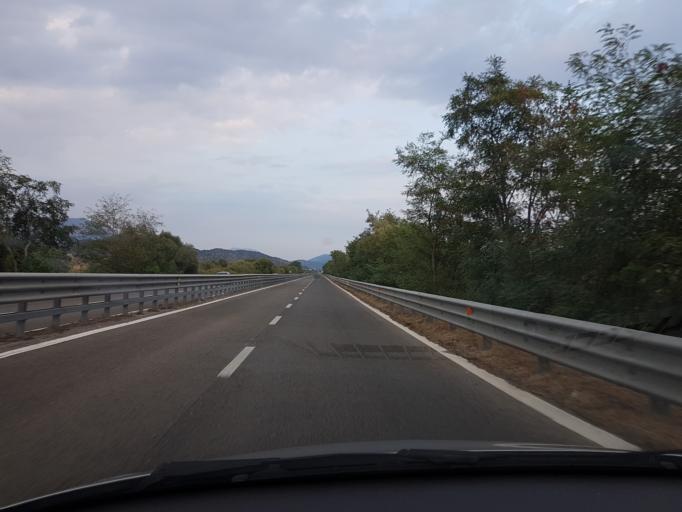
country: IT
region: Sardinia
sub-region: Provincia di Nuoro
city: Orune
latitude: 40.3842
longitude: 9.4425
